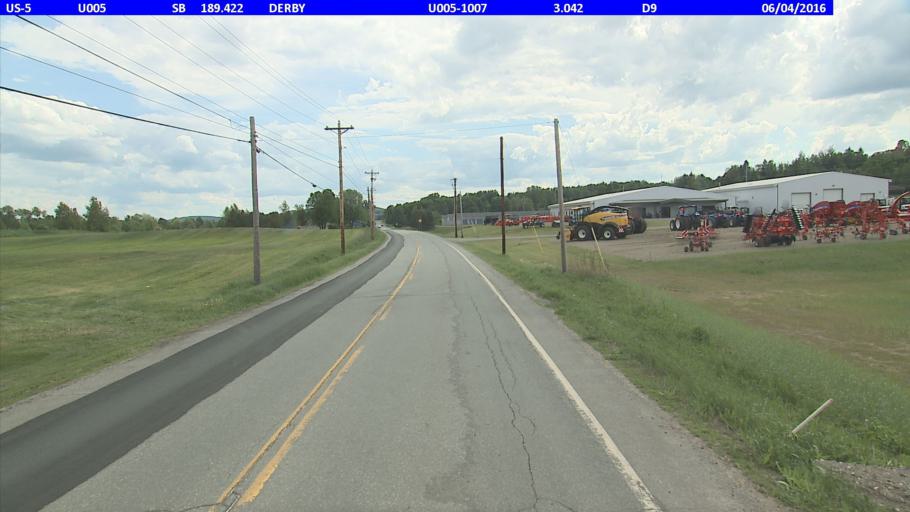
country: US
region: Vermont
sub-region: Orleans County
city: Newport
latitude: 44.9682
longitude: -72.1223
